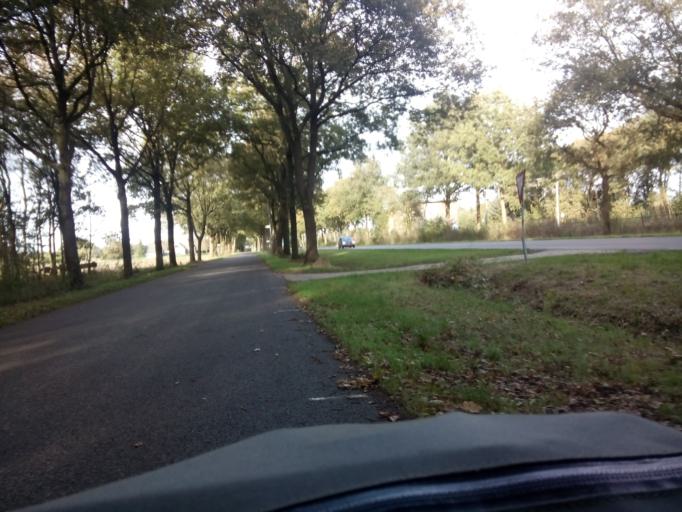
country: NL
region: Drenthe
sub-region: Gemeente Assen
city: Assen
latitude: 52.9126
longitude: 6.5415
